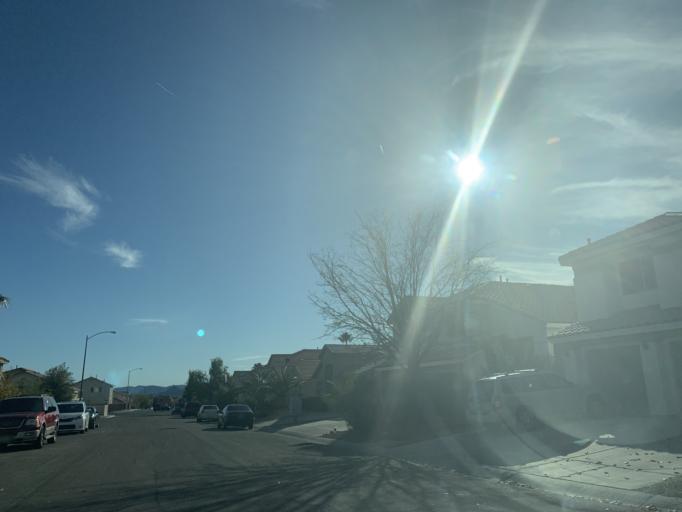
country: US
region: Nevada
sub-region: Clark County
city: Summerlin South
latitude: 36.1272
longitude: -115.2986
